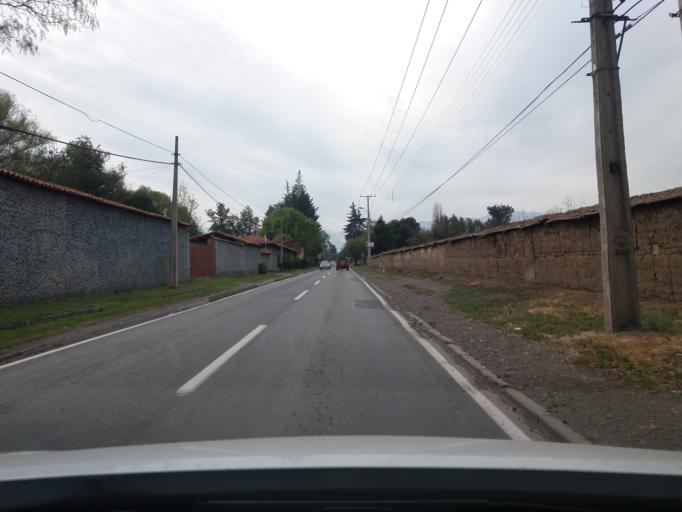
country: CL
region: Valparaiso
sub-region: Provincia de San Felipe
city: San Felipe
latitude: -32.8171
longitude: -70.6896
